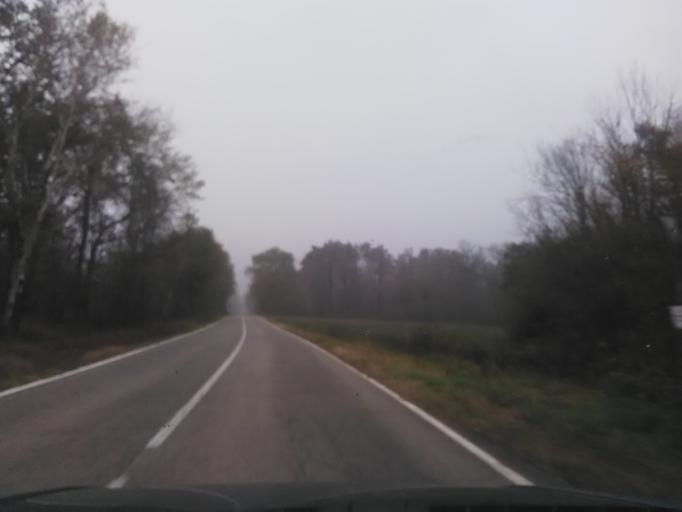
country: IT
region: Piedmont
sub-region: Provincia di Vercelli
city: San Maurizio
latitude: 45.5805
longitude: 8.2947
